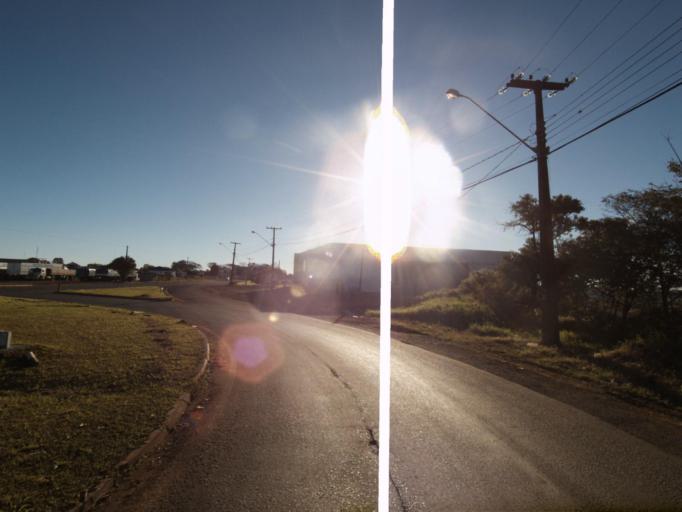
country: AR
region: Misiones
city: Bernardo de Irigoyen
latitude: -26.2575
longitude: -53.6185
